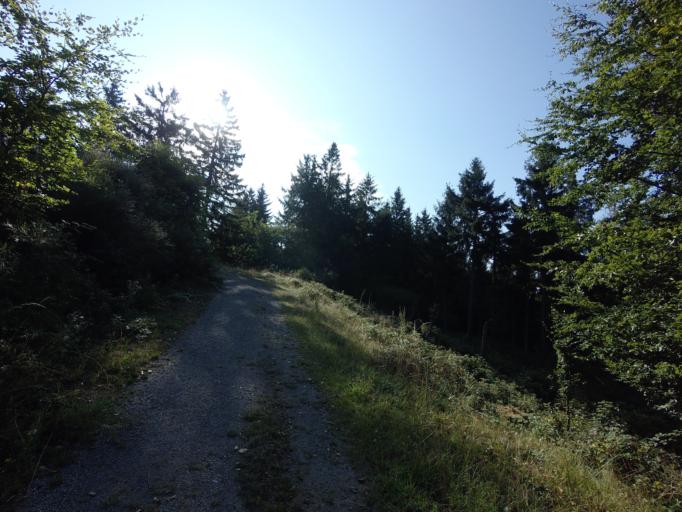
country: DE
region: North Rhine-Westphalia
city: Heimbach
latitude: 50.6104
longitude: 6.4103
